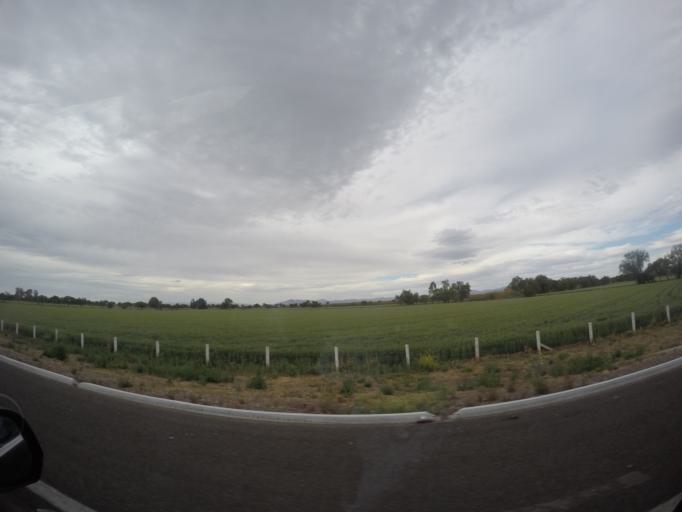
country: MX
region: Guanajuato
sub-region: Irapuato
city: Serrano
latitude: 20.7808
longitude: -101.4107
